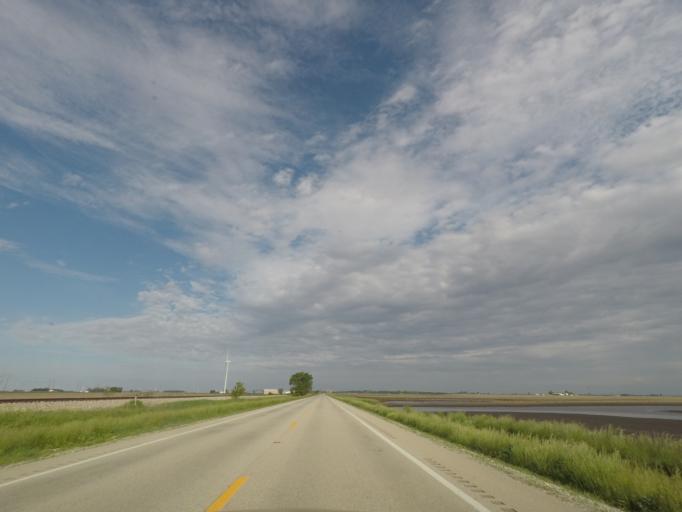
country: US
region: Illinois
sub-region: Logan County
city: Mount Pulaski
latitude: 39.9910
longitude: -89.2416
